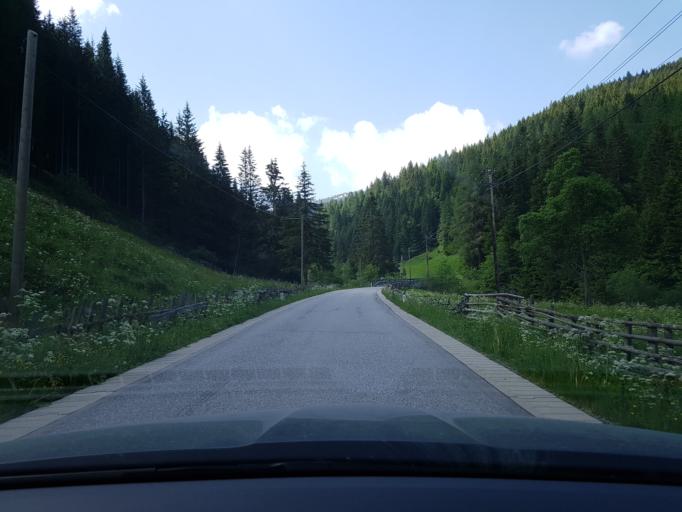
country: AT
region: Salzburg
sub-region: Politischer Bezirk Tamsweg
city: Thomatal
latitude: 47.0499
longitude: 13.7113
